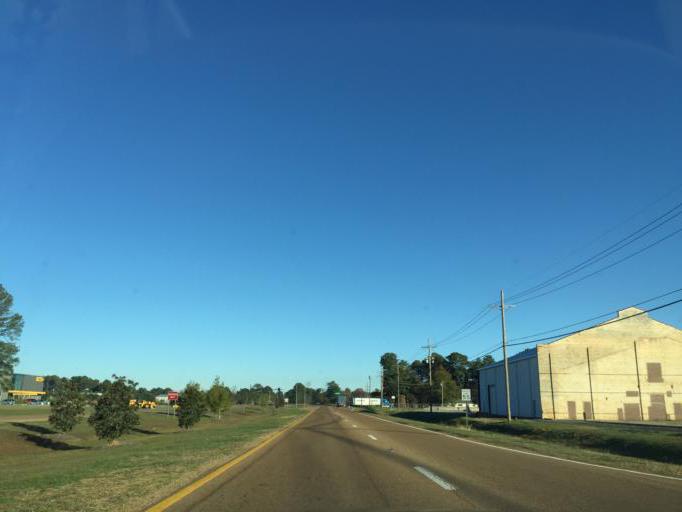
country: US
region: Mississippi
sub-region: Rankin County
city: Flowood
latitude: 32.3048
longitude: -90.1413
